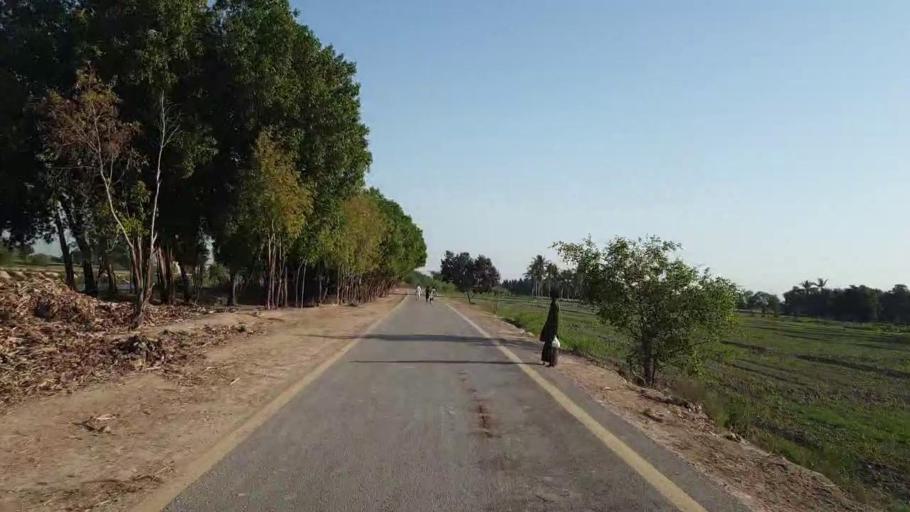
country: PK
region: Sindh
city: Hyderabad
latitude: 25.3347
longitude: 68.4223
